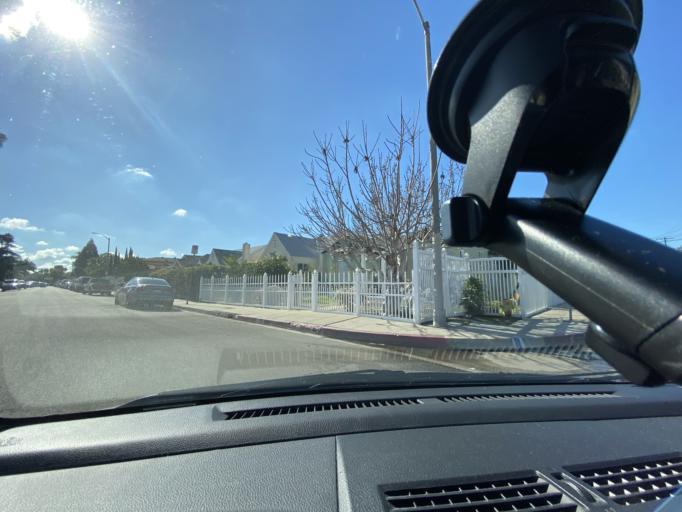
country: US
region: California
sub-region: Los Angeles County
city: Culver City
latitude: 34.0408
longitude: -118.3790
